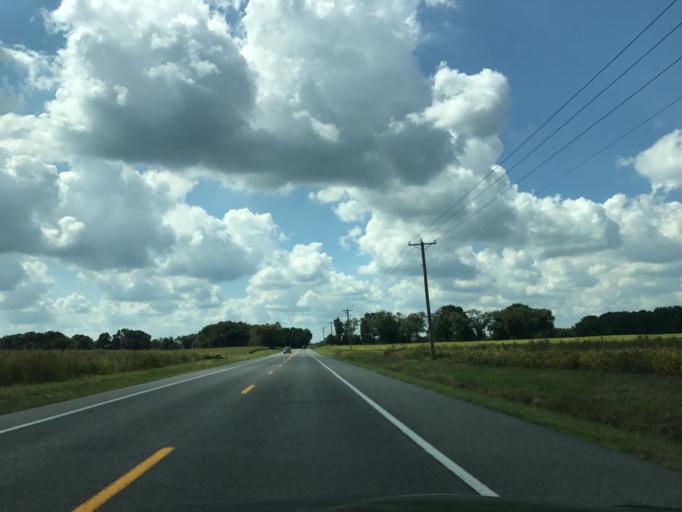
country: US
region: Maryland
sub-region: Caroline County
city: Greensboro
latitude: 39.1417
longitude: -75.7508
